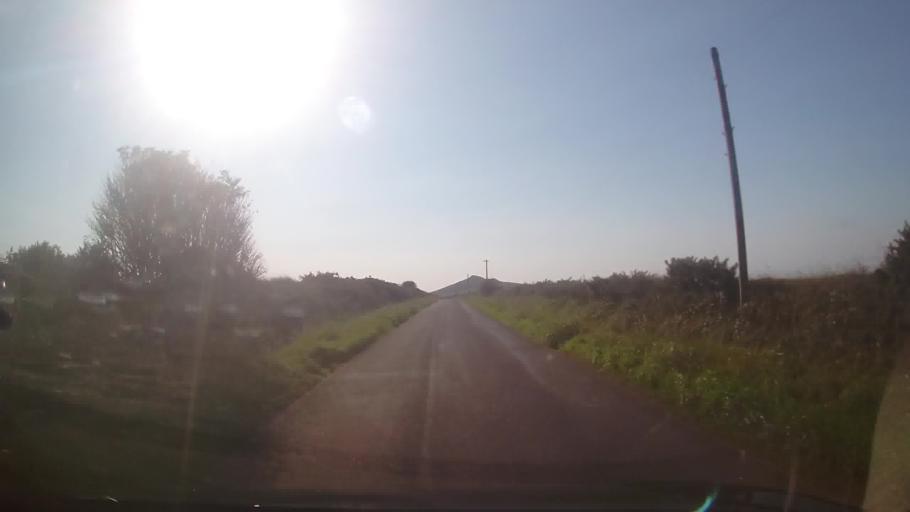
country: GB
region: Wales
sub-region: Pembrokeshire
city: Llanrhian
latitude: 51.9208
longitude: -5.2178
